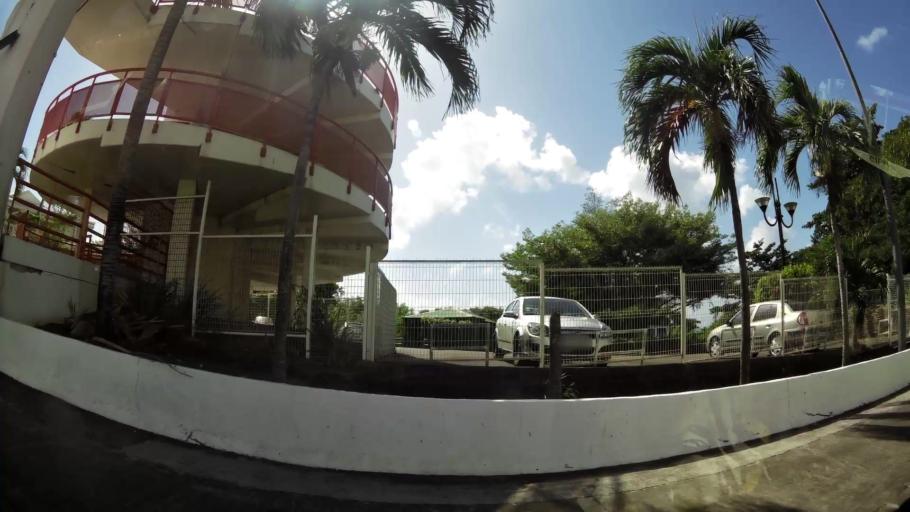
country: MQ
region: Martinique
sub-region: Martinique
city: Fort-de-France
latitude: 14.6080
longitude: -61.0943
